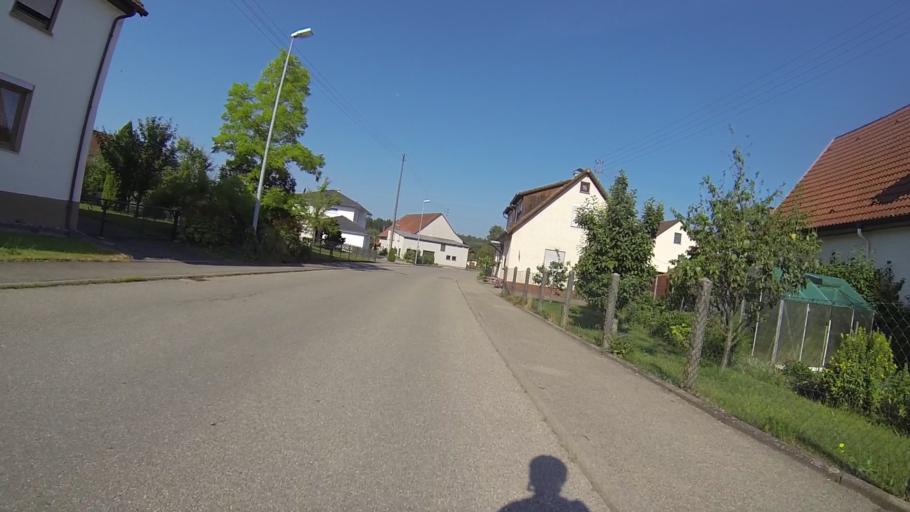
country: DE
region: Baden-Wuerttemberg
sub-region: Regierungsbezirk Stuttgart
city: Konigsbronn
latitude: 48.7482
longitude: 10.1435
